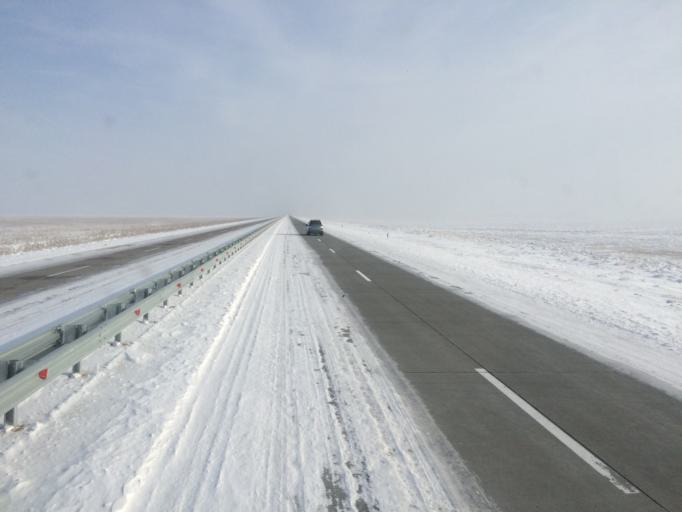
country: KZ
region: Zhambyl
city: Georgiyevka
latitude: 43.3447
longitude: 74.3395
